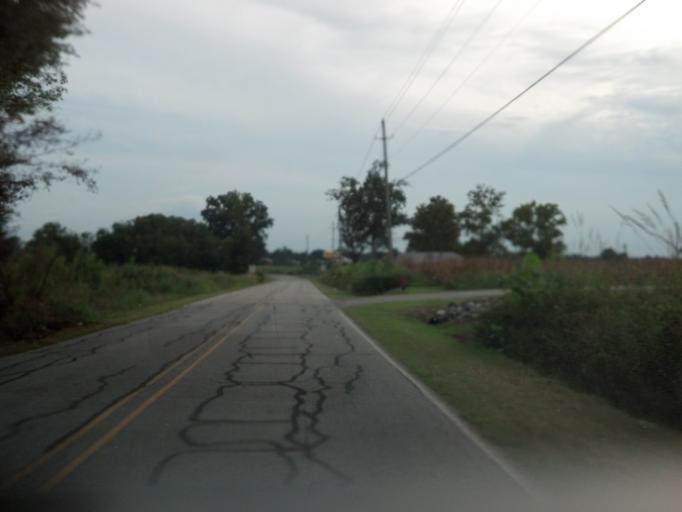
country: US
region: North Carolina
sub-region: Pitt County
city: Ayden
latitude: 35.4837
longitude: -77.4295
